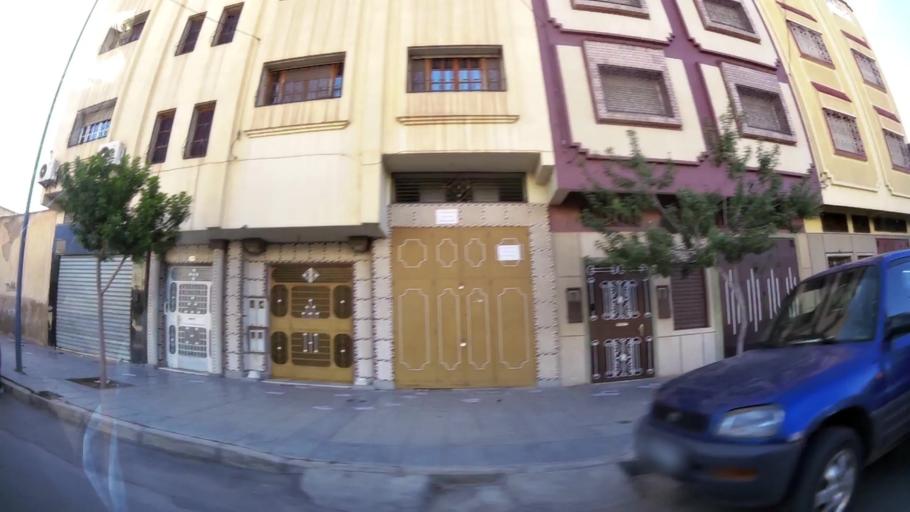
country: MA
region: Oriental
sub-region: Oujda-Angad
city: Oujda
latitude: 34.6932
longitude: -1.9123
